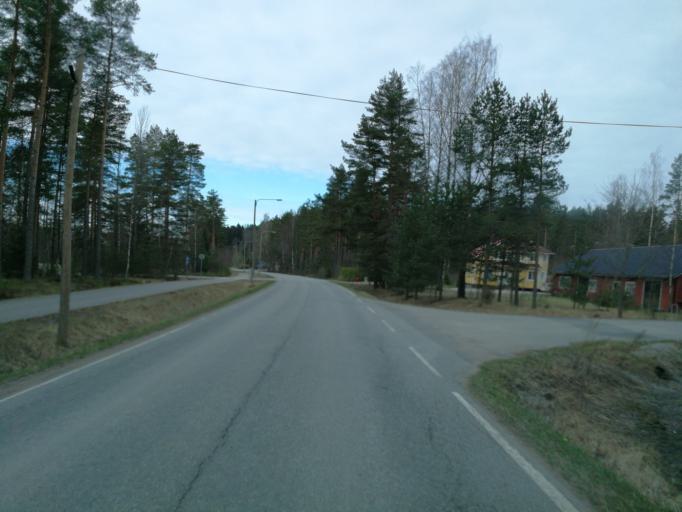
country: FI
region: Varsinais-Suomi
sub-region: Salo
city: Muurla
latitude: 60.3672
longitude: 23.3000
